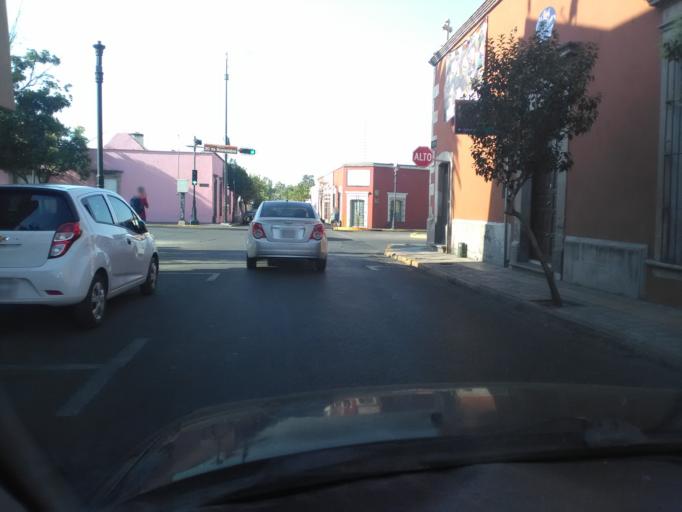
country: MX
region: Durango
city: Victoria de Durango
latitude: 24.0244
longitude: -104.6742
